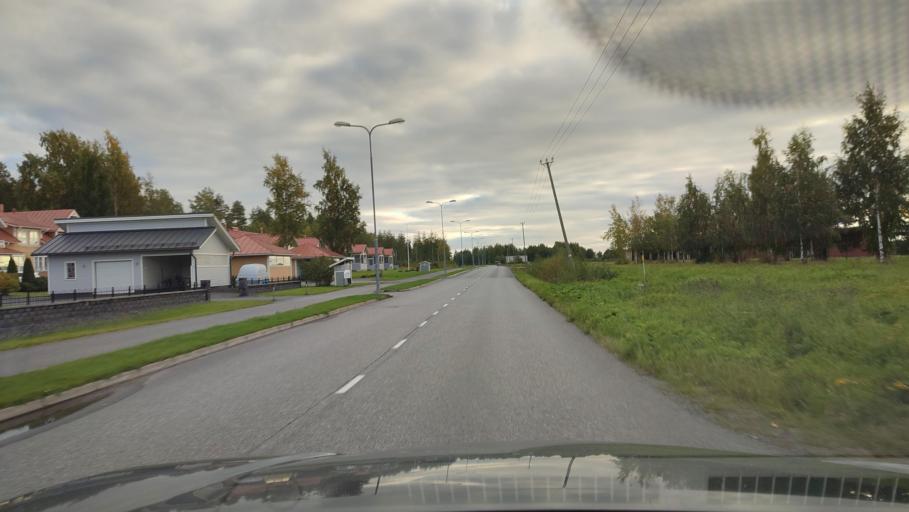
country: FI
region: Ostrobothnia
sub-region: Sydosterbotten
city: Kristinestad
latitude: 62.2678
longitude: 21.3863
